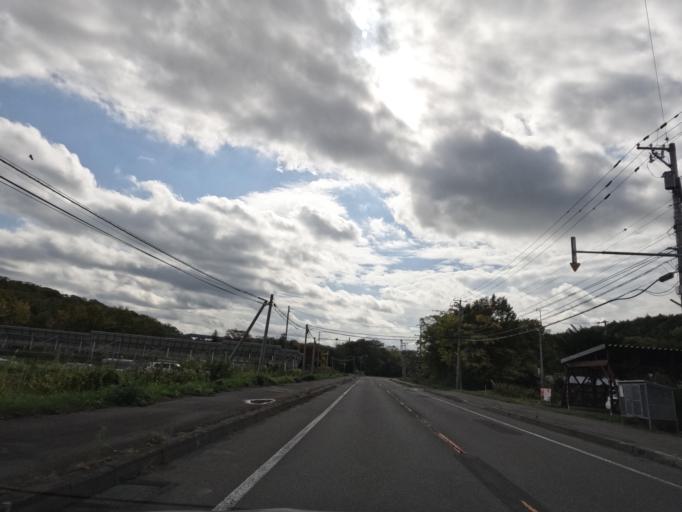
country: JP
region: Hokkaido
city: Chitose
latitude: 42.8149
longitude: 141.5939
